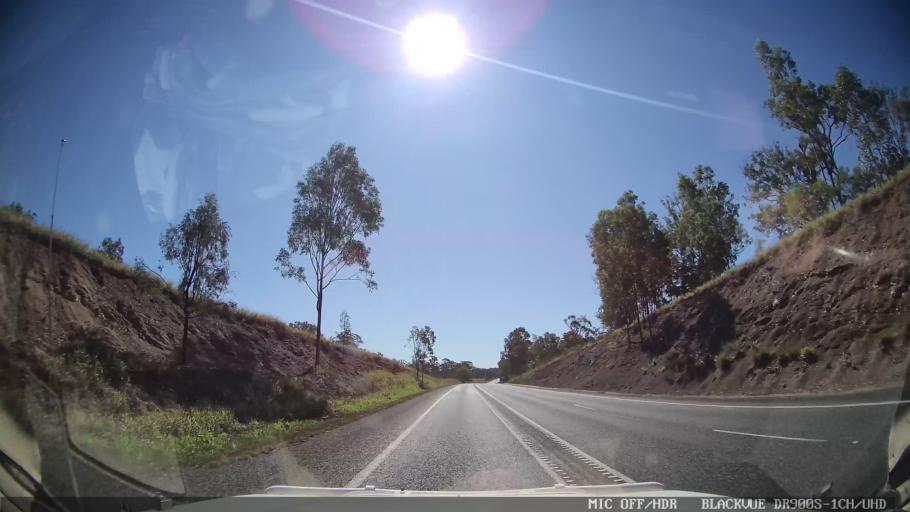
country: AU
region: Queensland
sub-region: Fraser Coast
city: Maryborough
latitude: -25.7723
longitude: 152.5966
